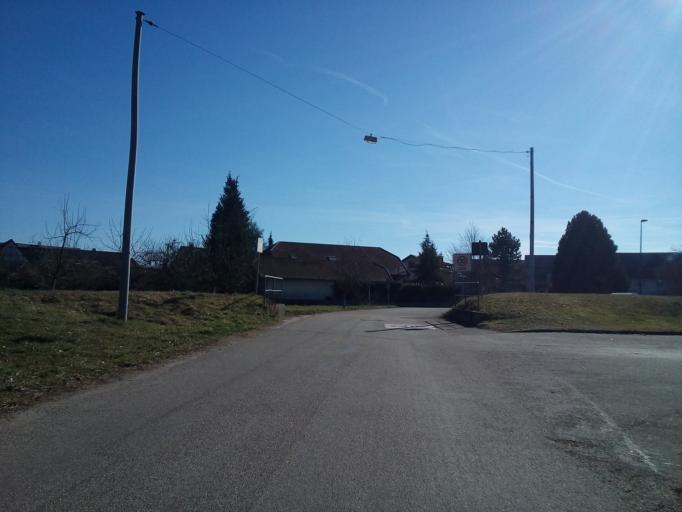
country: FR
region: Alsace
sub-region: Departement du Bas-Rhin
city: Gambsheim
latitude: 48.6505
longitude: 7.8887
